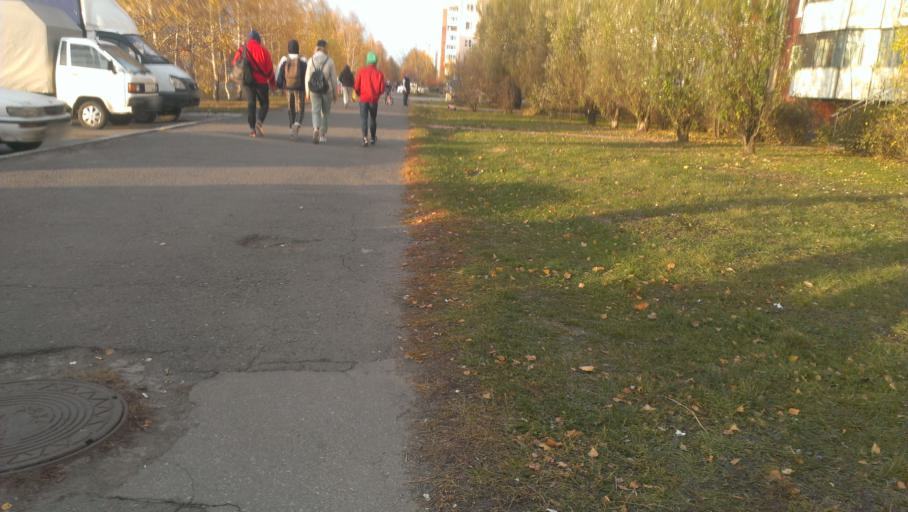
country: RU
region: Altai Krai
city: Novosilikatnyy
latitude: 53.3375
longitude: 83.6699
